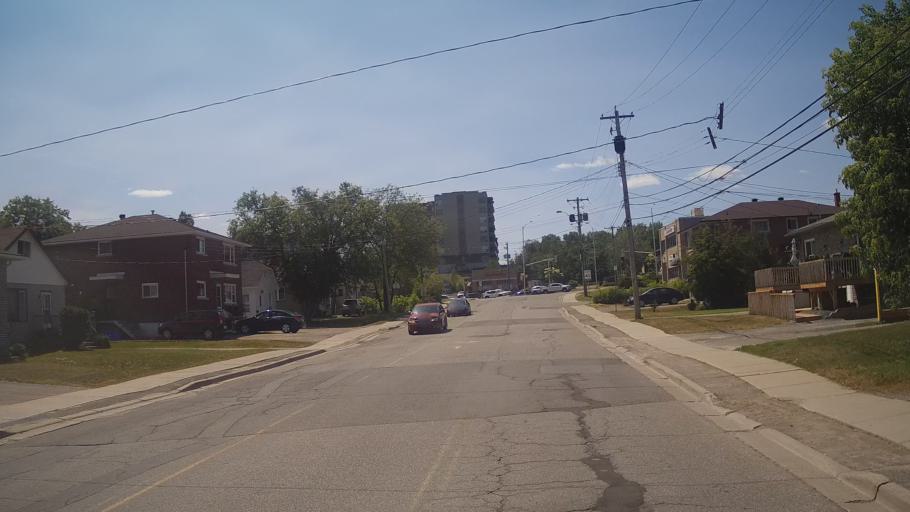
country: CA
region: Ontario
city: Greater Sudbury
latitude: 46.4636
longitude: -81.0064
